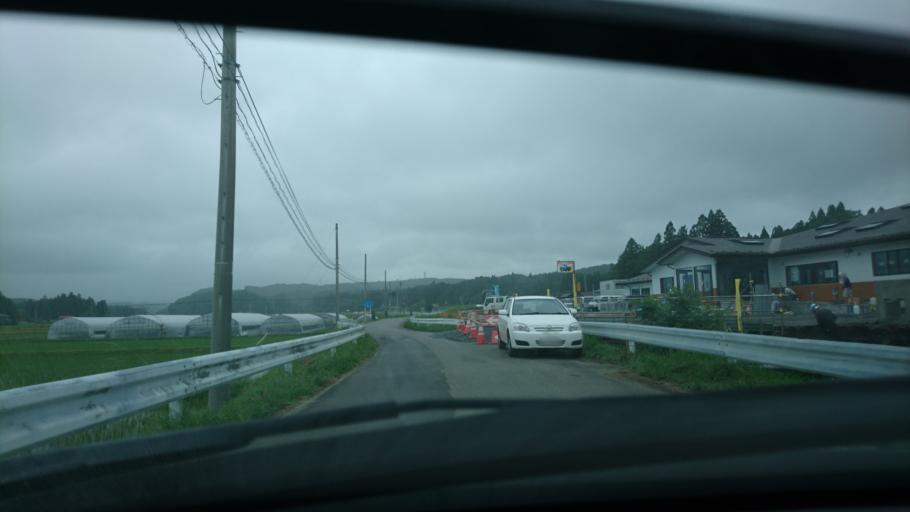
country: JP
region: Iwate
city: Ichinoseki
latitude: 38.9492
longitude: 141.0532
